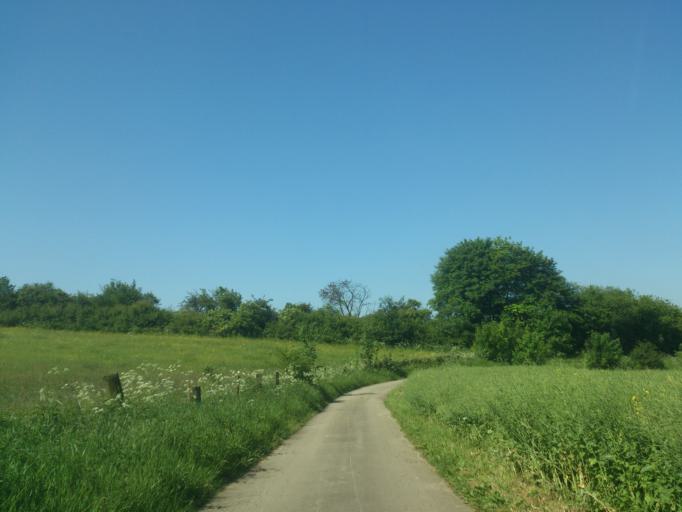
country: DE
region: North Rhine-Westphalia
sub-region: Regierungsbezirk Detmold
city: Bad Driburg
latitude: 51.6941
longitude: 8.9976
